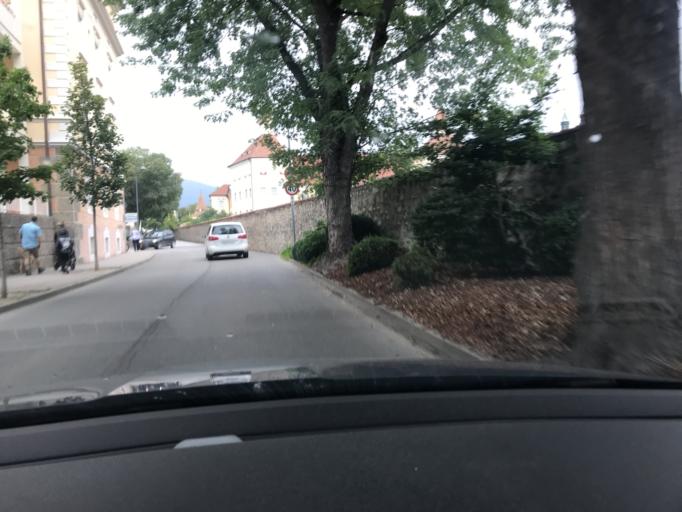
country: IT
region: Trentino-Alto Adige
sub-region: Bolzano
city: Bressanone
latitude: 46.7132
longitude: 11.6554
